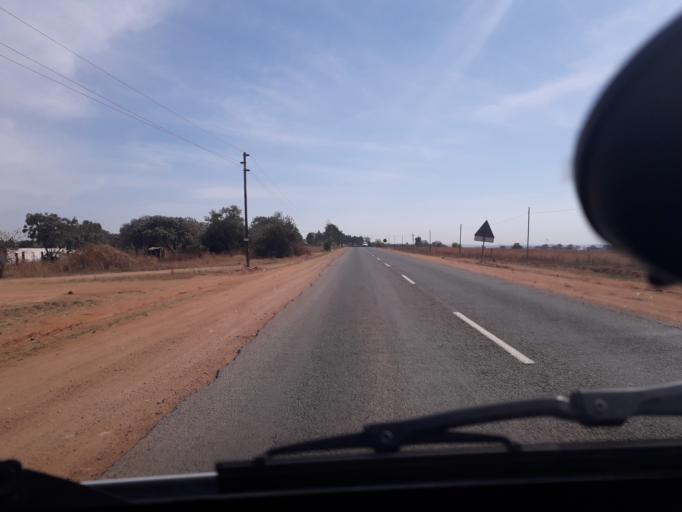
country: ZA
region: Gauteng
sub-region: West Rand District Municipality
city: Muldersdriseloop
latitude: -26.0034
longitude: 27.8579
